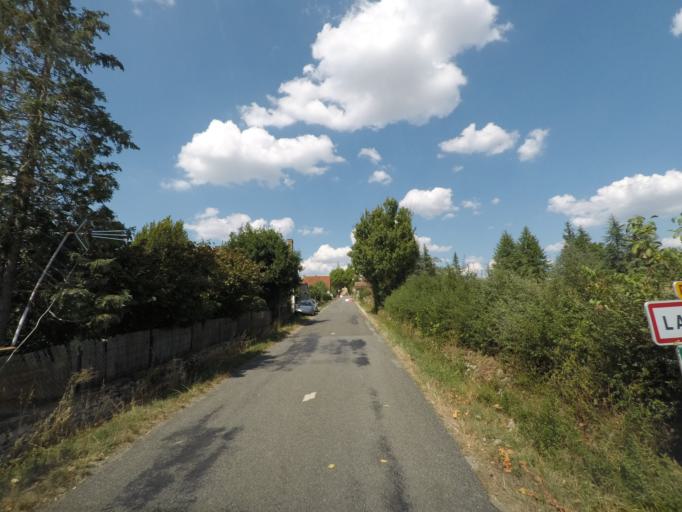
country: FR
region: Midi-Pyrenees
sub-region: Departement du Lot
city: Cahors
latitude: 44.5657
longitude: 1.5814
